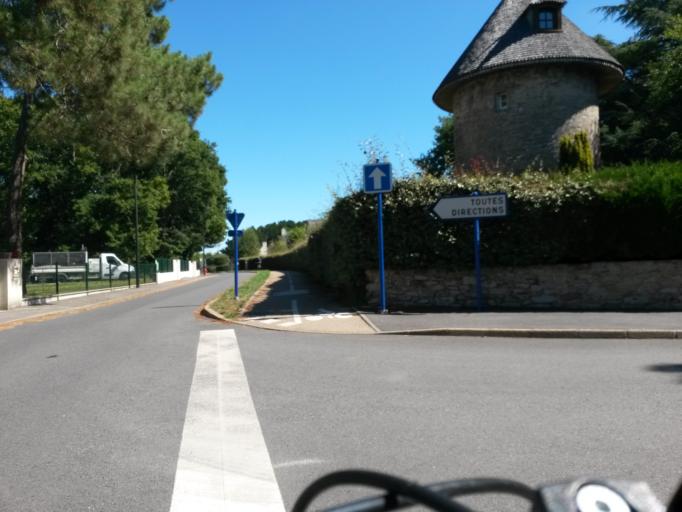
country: FR
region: Pays de la Loire
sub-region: Departement de la Loire-Atlantique
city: Mesquer
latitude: 47.4016
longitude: -2.4606
